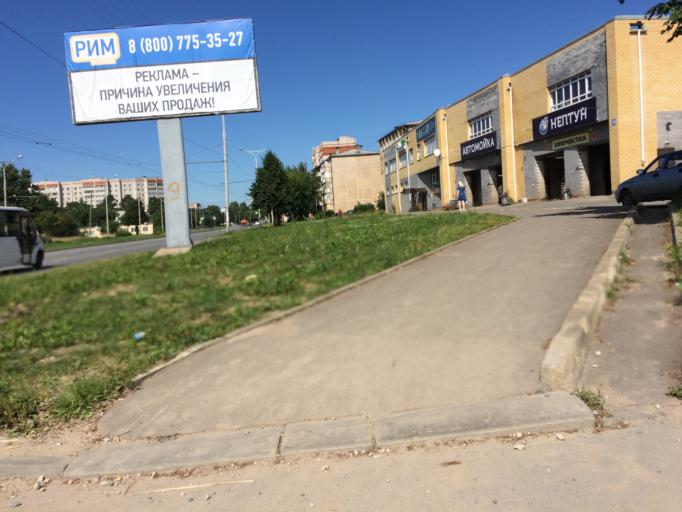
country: RU
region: Mariy-El
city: Yoshkar-Ola
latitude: 56.6294
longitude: 47.9378
